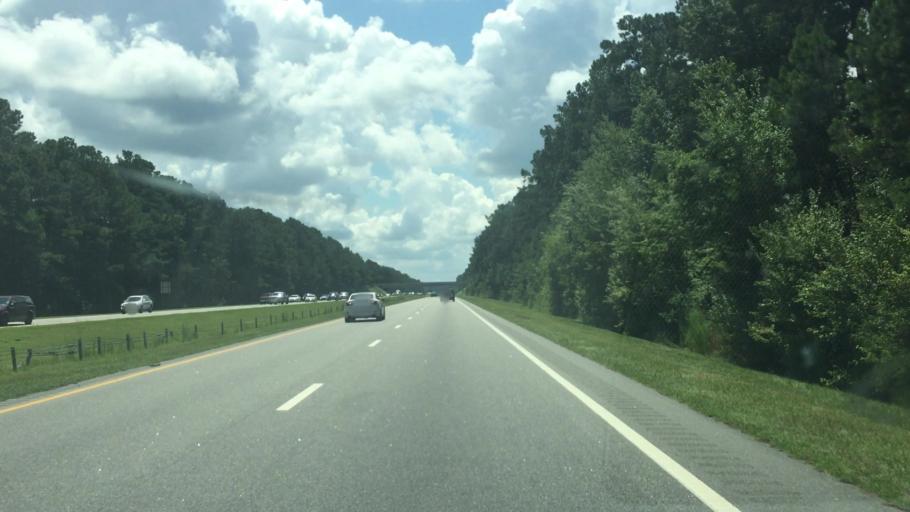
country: US
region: North Carolina
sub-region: Robeson County
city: Lumberton
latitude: 34.5497
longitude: -79.0233
